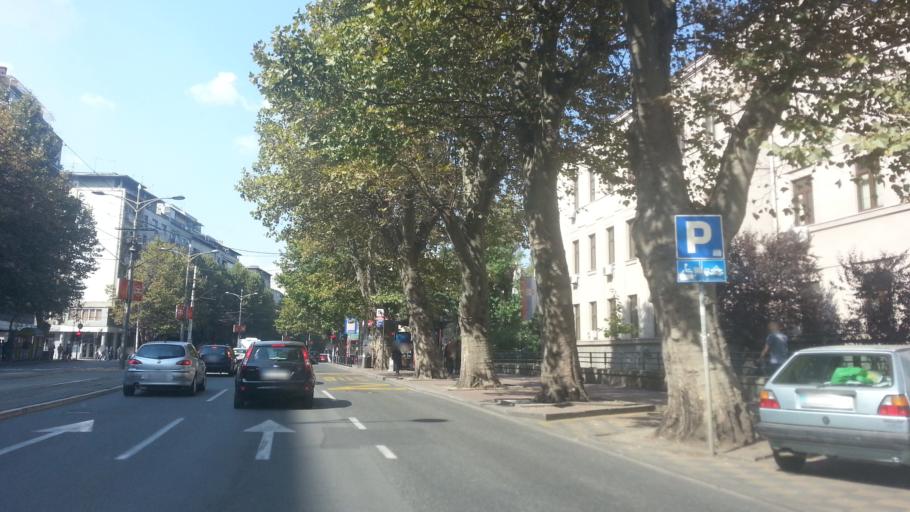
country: RS
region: Central Serbia
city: Belgrade
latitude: 44.8067
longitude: 20.4728
